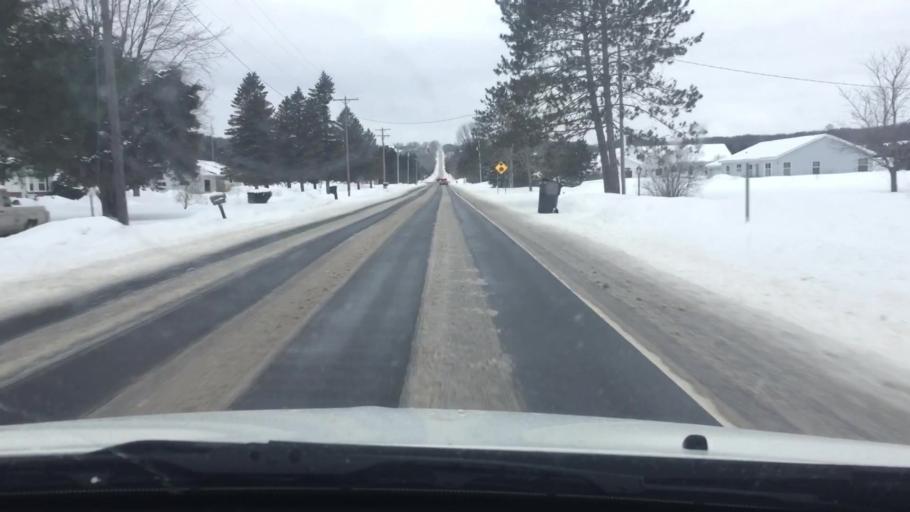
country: US
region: Michigan
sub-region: Charlevoix County
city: East Jordan
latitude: 45.1326
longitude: -85.1345
